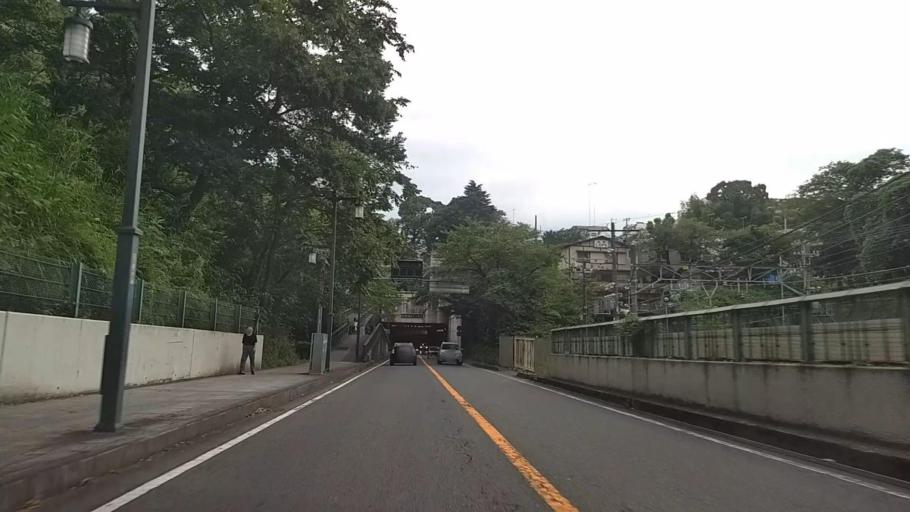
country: JP
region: Kanagawa
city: Odawara
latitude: 35.2510
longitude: 139.1523
